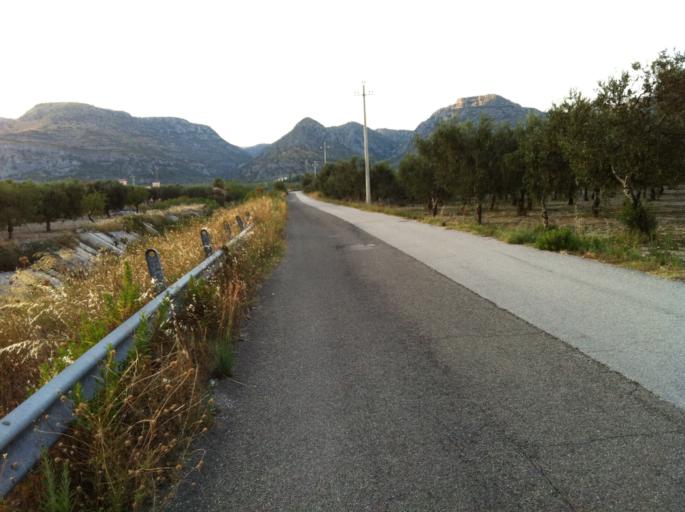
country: IT
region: Apulia
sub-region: Provincia di Foggia
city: Monte Sant'Angelo
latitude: 41.6597
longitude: 15.9503
